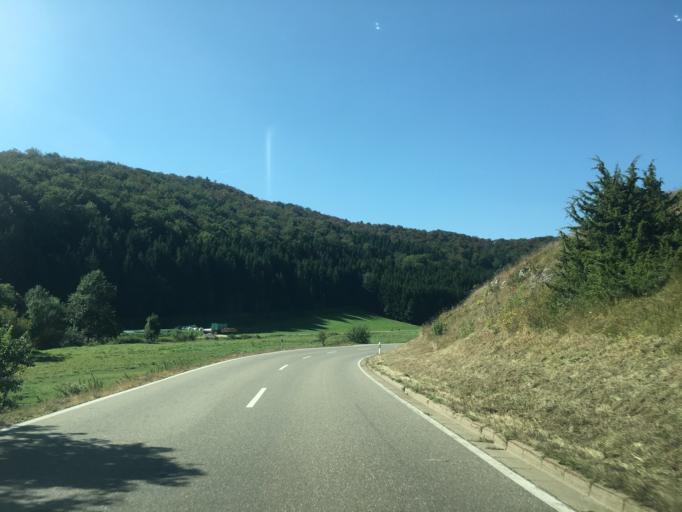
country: DE
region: Baden-Wuerttemberg
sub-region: Tuebingen Region
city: Hayingen
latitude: 48.3344
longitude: 9.5004
